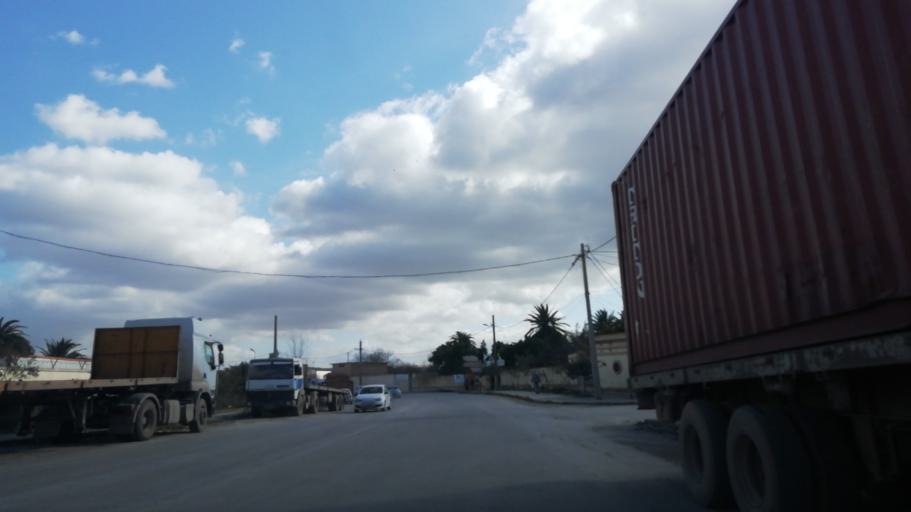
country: DZ
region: Oran
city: Es Senia
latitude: 35.6488
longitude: -0.6087
